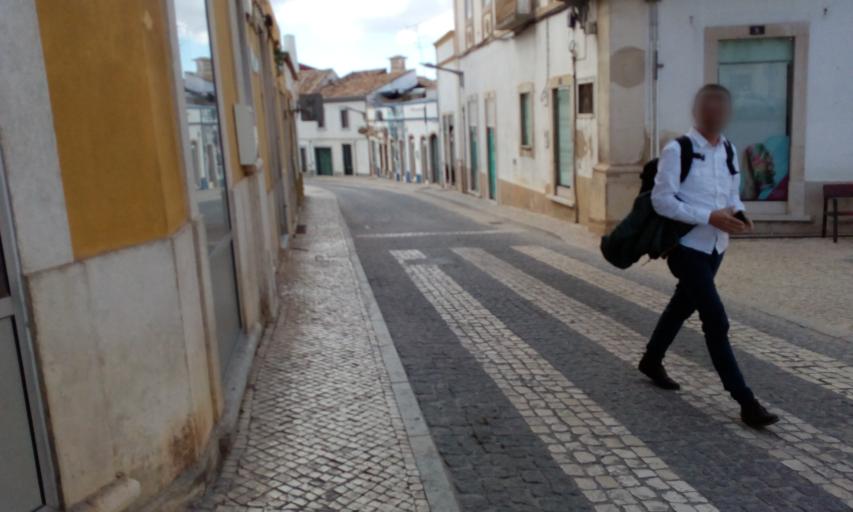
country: PT
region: Faro
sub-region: Loule
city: Loule
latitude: 37.1399
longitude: -8.0234
